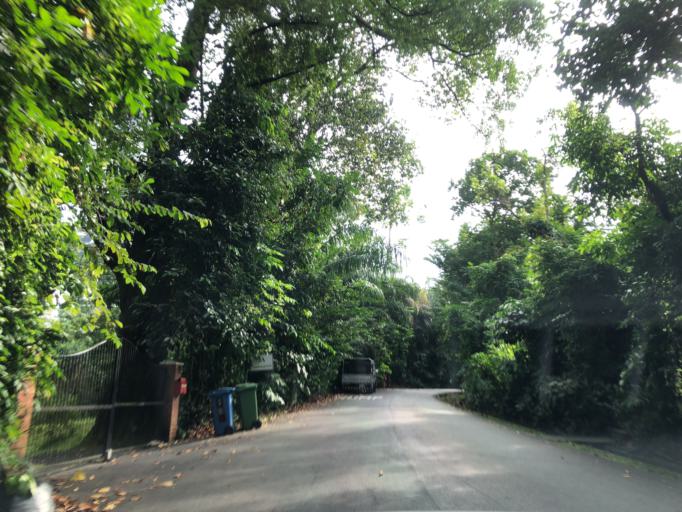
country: SG
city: Singapore
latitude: 1.3127
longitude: 103.8352
